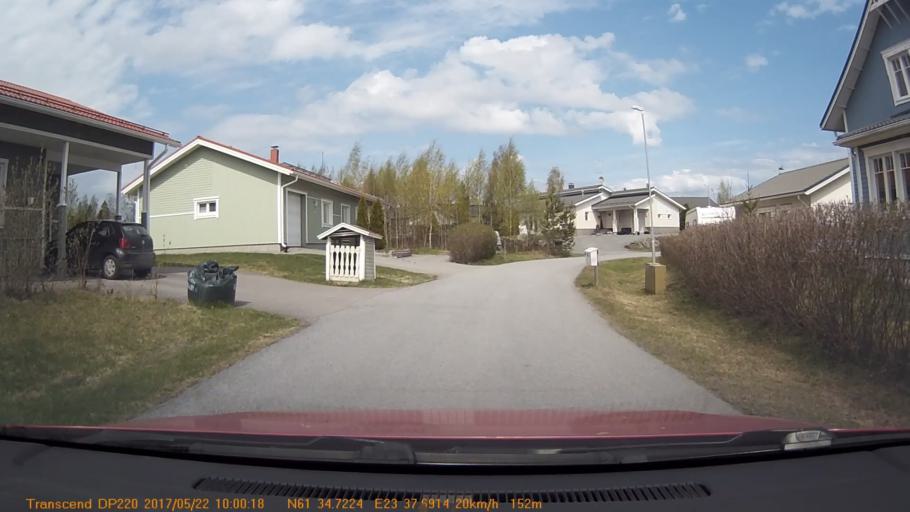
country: FI
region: Pirkanmaa
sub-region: Tampere
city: Yloejaervi
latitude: 61.5787
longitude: 23.6282
